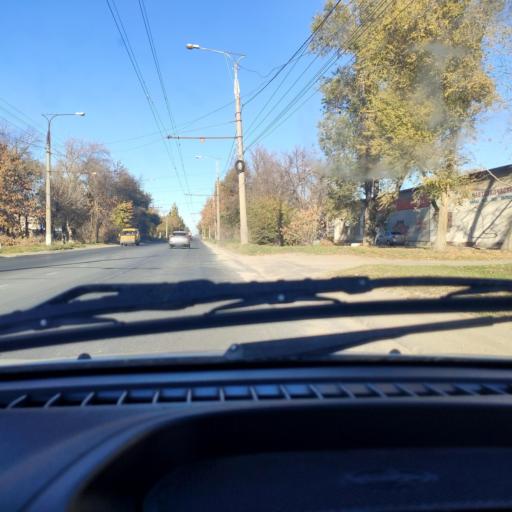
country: RU
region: Samara
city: Tol'yatti
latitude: 53.5635
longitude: 49.4557
